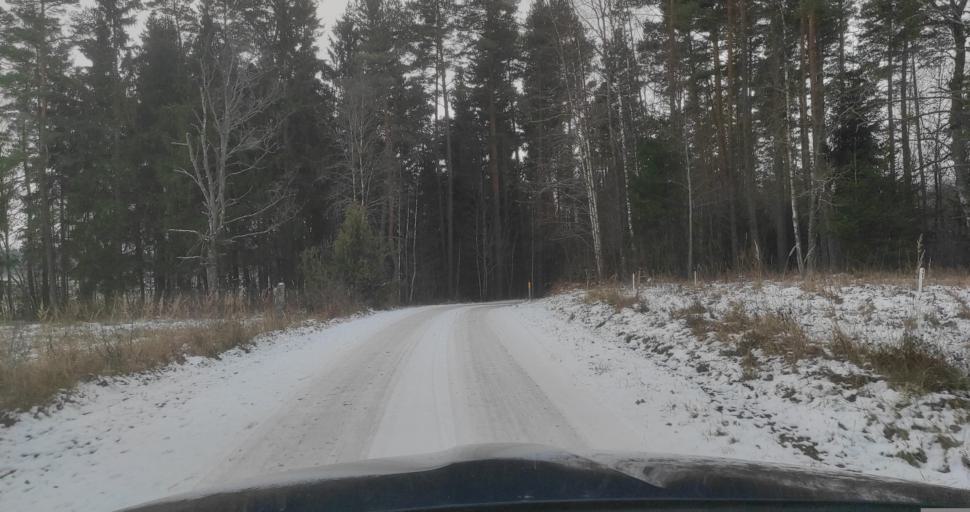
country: LV
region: Kuldigas Rajons
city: Kuldiga
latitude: 56.9931
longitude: 21.8071
